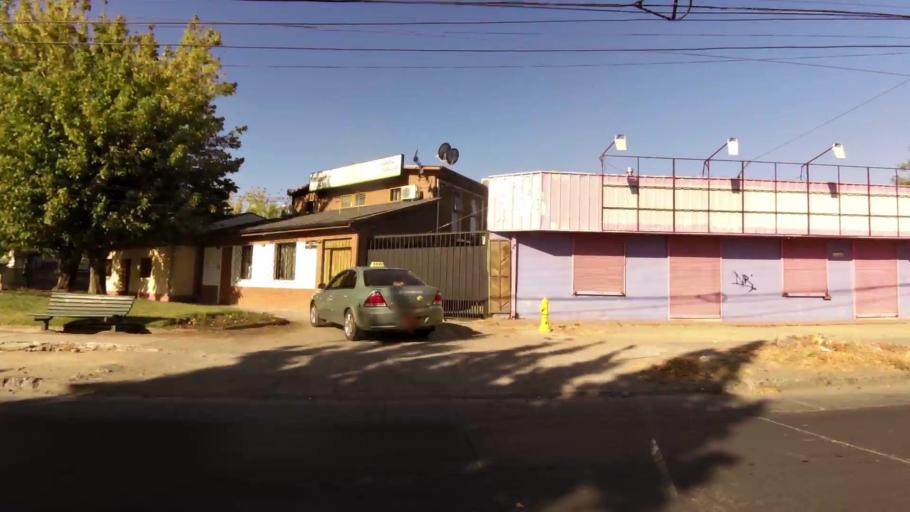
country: CL
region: Maule
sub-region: Provincia de Talca
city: Talca
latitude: -35.4177
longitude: -71.6535
